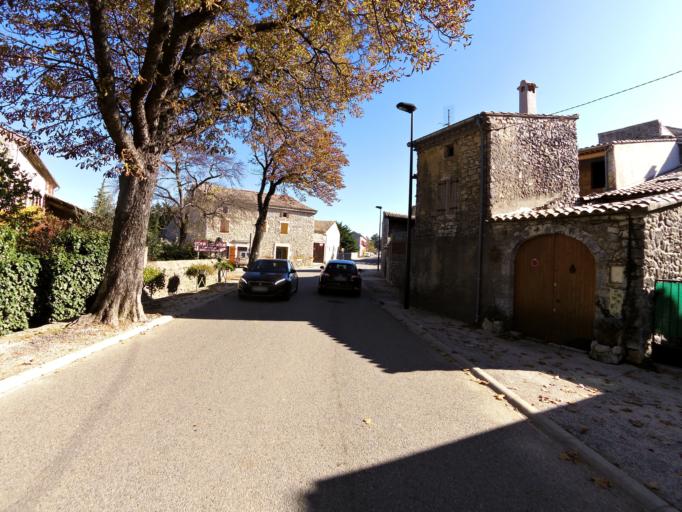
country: FR
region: Languedoc-Roussillon
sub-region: Departement du Gard
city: Saint-Julien-de-Peyrolas
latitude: 44.3932
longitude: 4.5022
